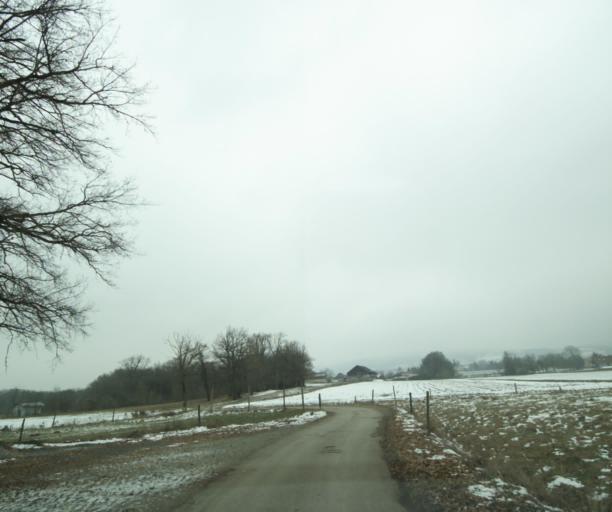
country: FR
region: Rhone-Alpes
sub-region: Departement de la Haute-Savoie
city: Reignier-Esery
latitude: 46.1314
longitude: 6.2864
